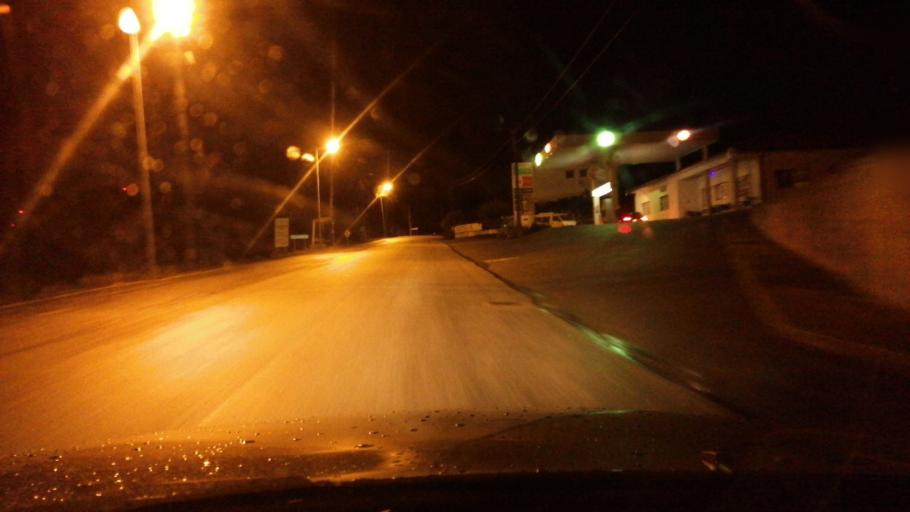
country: PT
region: Viseu
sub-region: Armamar
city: Armamar
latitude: 41.0666
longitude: -7.6469
